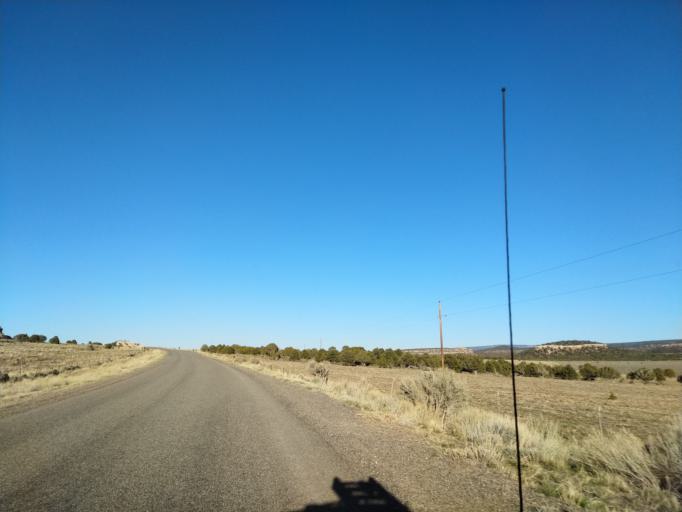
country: US
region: Colorado
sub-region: Mesa County
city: Loma
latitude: 38.9489
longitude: -108.9611
